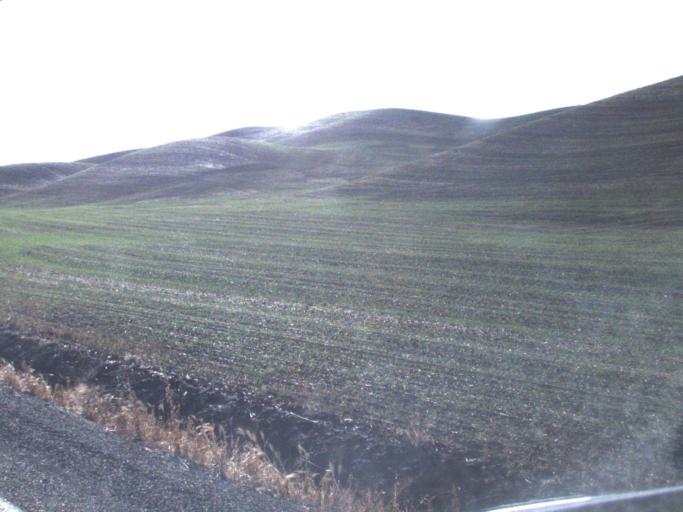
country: US
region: Washington
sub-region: Whitman County
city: Colfax
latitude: 46.7621
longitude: -117.3842
